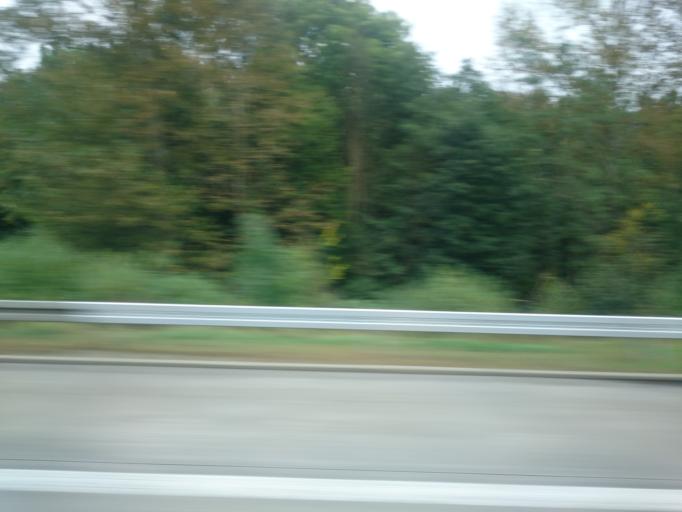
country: DE
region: Saxony-Anhalt
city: Ermlitz
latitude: 51.3746
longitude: 12.1864
